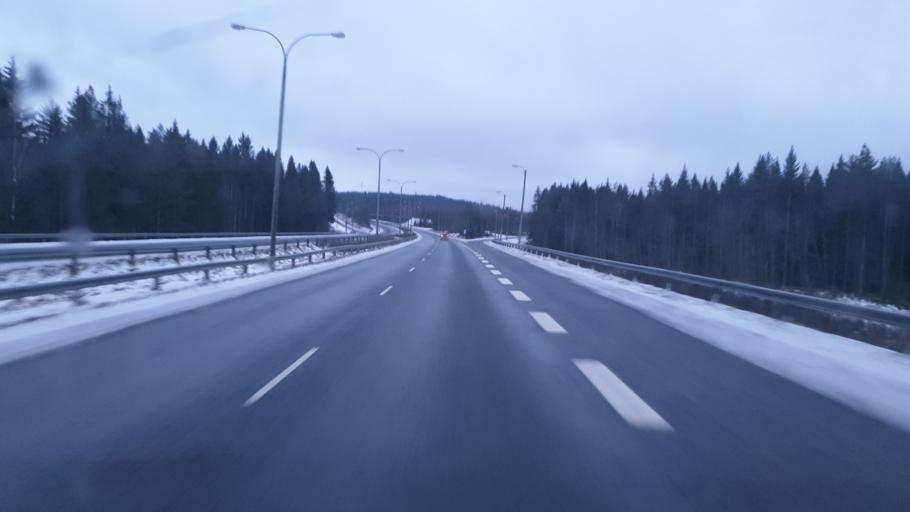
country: FI
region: Northern Savo
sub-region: Kuopio
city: Siilinjaervi
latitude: 63.0230
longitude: 27.6591
